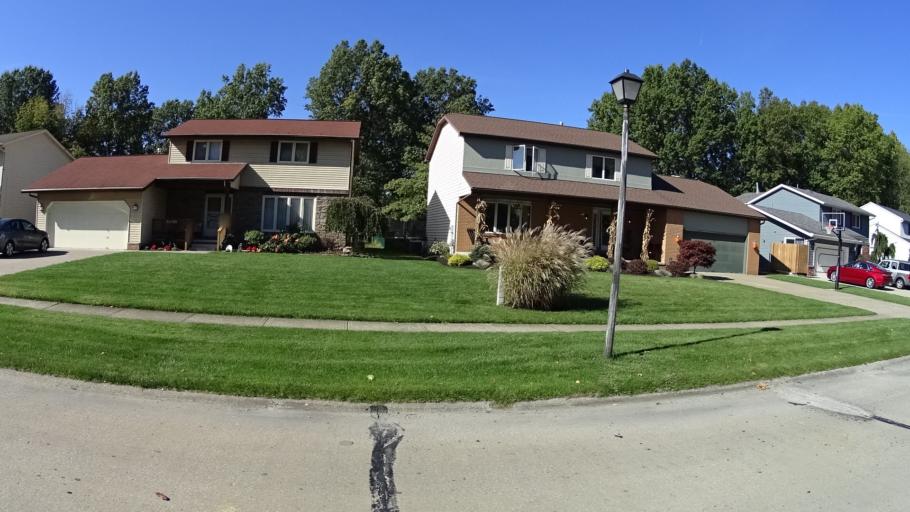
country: US
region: Ohio
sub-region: Lorain County
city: Lorain
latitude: 41.4155
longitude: -82.1750
